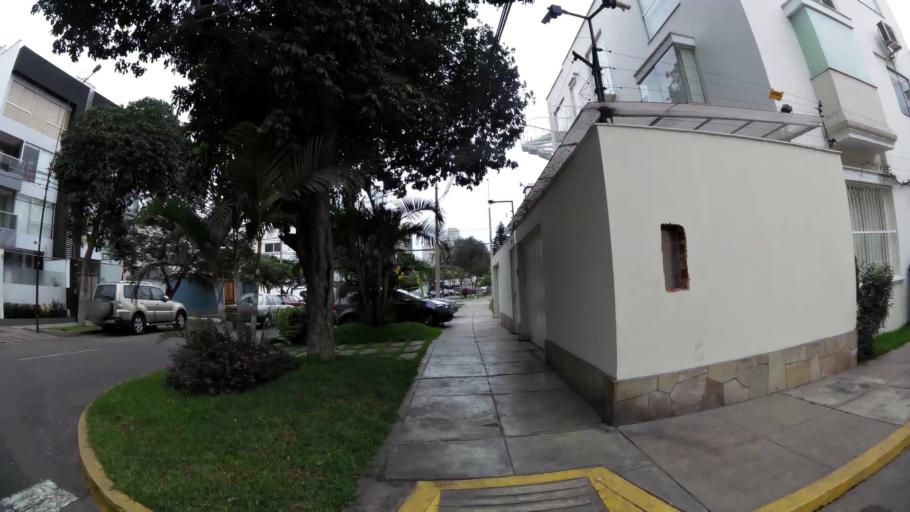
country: PE
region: Lima
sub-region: Lima
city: Surco
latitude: -12.1255
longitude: -77.0201
